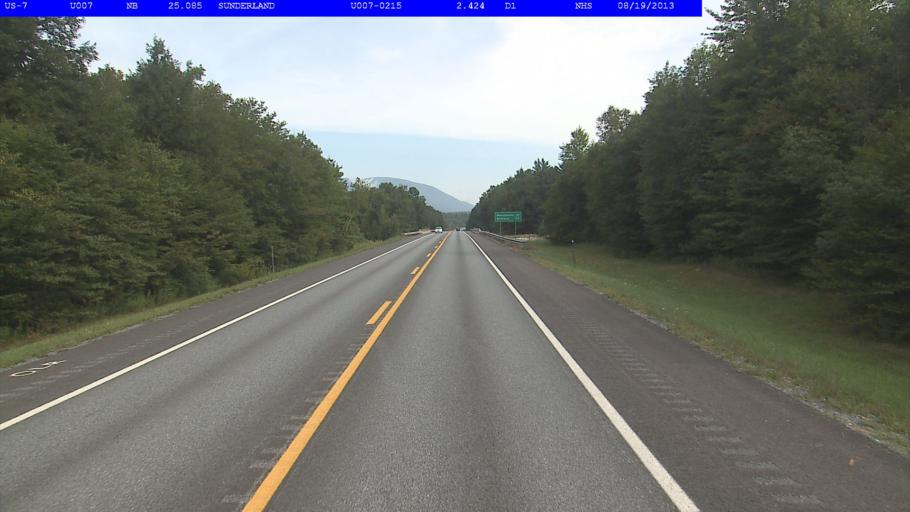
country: US
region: Vermont
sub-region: Bennington County
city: Arlington
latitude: 43.0592
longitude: -73.1255
